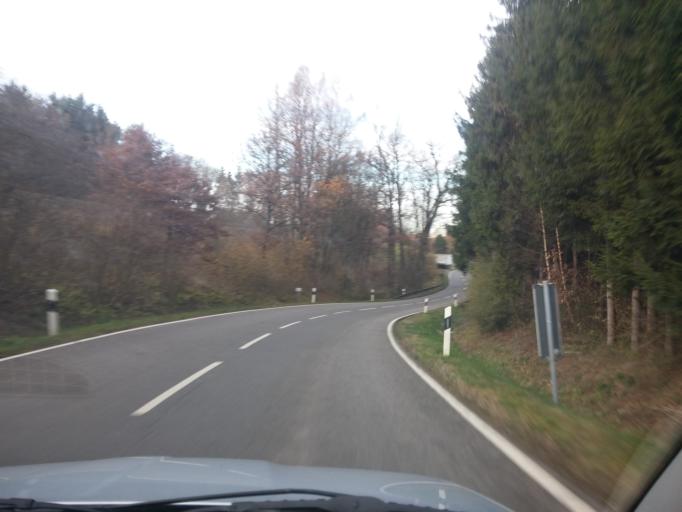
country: DE
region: Bavaria
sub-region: Upper Bavaria
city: Ottenhofen
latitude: 48.2270
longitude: 11.8881
